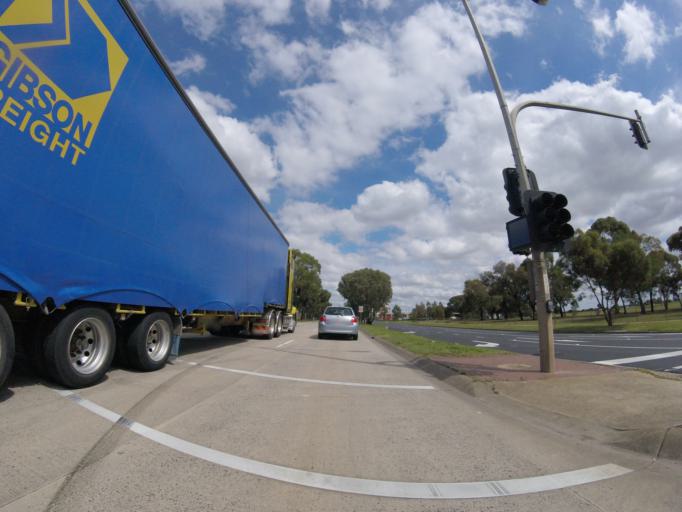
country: AU
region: Victoria
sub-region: Brimbank
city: Keilor Park
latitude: -37.7181
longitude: 144.8550
